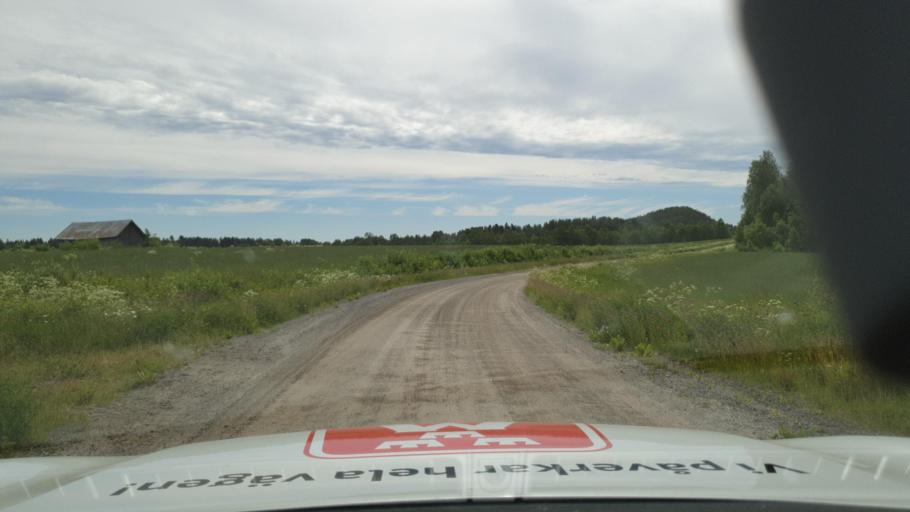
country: SE
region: Vaesterbotten
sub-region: Robertsfors Kommun
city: Robertsfors
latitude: 64.2645
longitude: 20.6413
